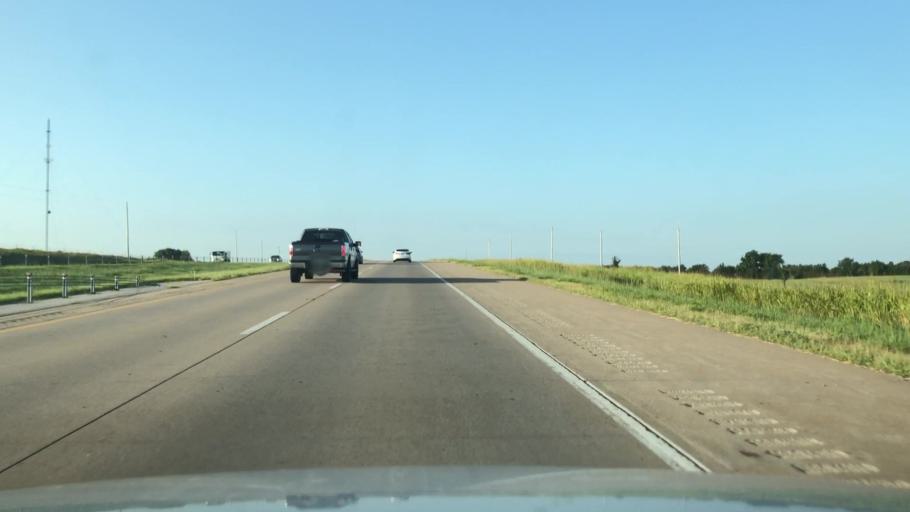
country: US
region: Oklahoma
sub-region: Washington County
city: Bartlesville
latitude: 36.6303
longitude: -95.9363
